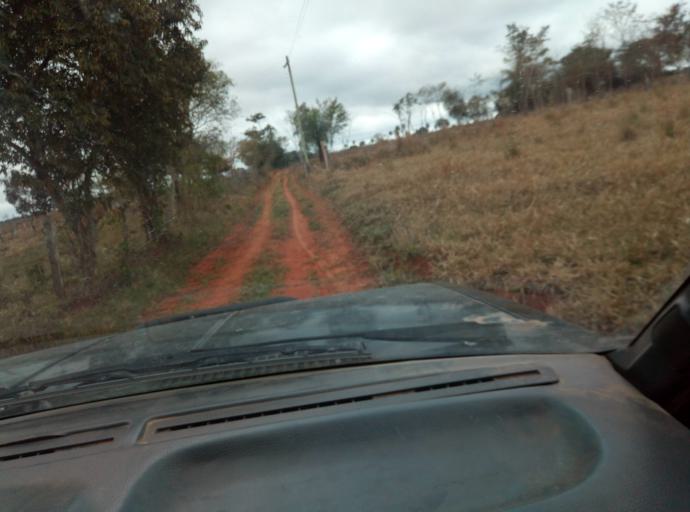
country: PY
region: Caaguazu
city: Doctor Cecilio Baez
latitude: -25.1452
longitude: -56.2930
